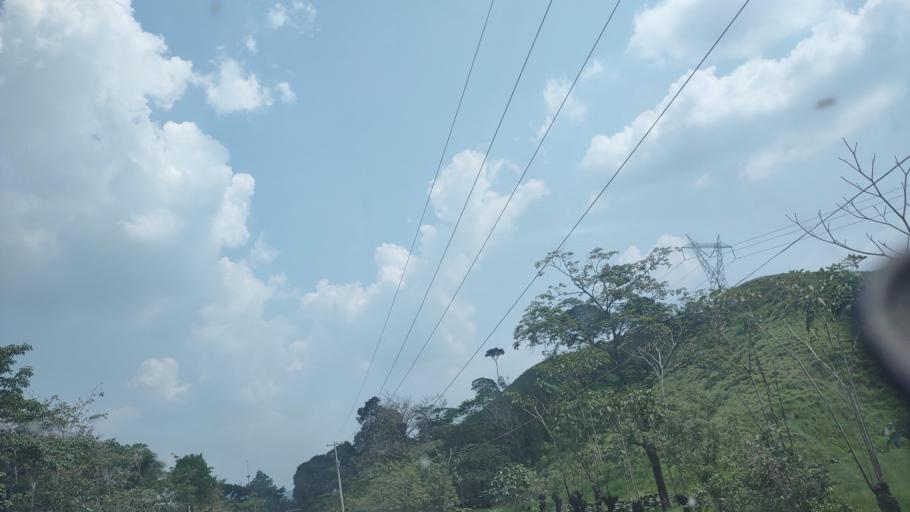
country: MX
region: Tabasco
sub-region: Huimanguillo
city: Francisco Rueda
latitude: 17.5949
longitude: -93.8986
